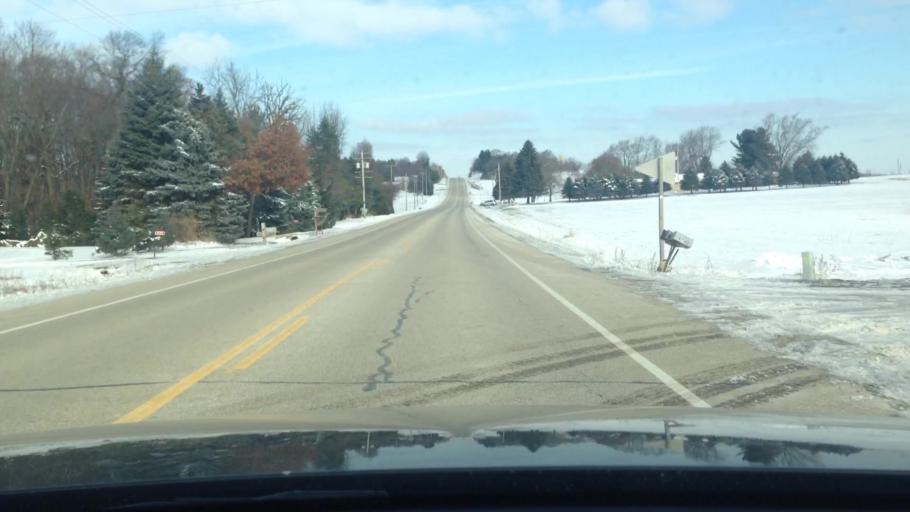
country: US
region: Wisconsin
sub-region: Walworth County
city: East Troy
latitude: 42.7506
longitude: -88.4063
